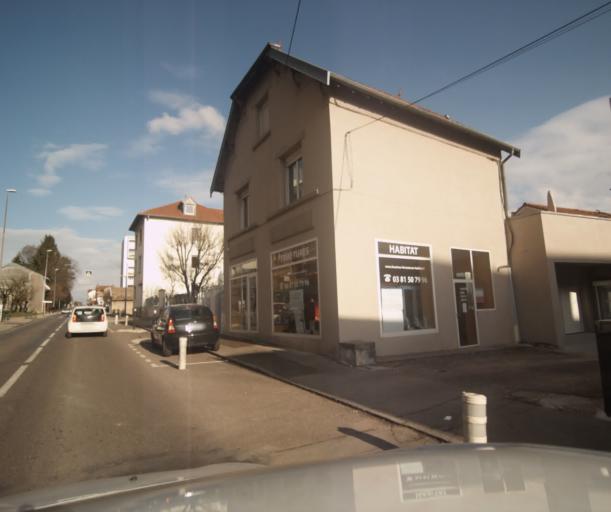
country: FR
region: Franche-Comte
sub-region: Departement du Doubs
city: Besancon
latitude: 47.2525
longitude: 6.0364
